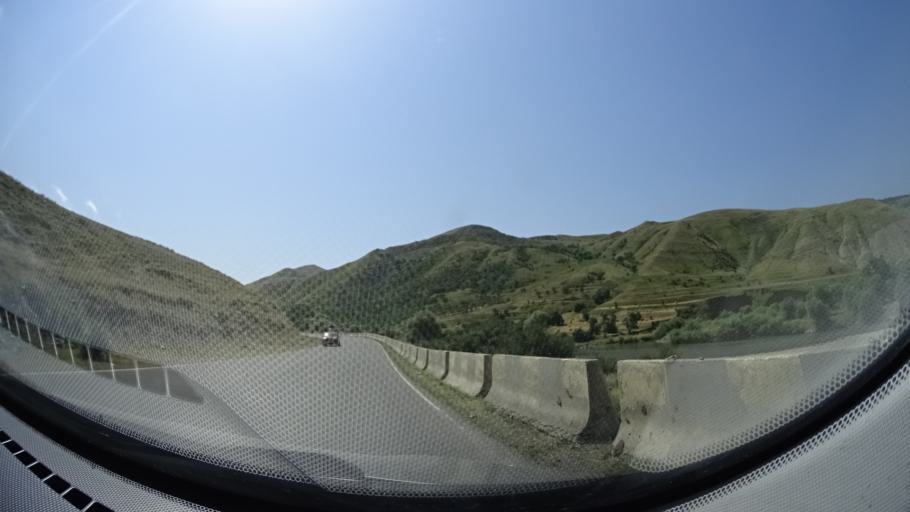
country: GE
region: Samtskhe-Javakheti
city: Aspindza
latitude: 41.5965
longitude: 43.1970
